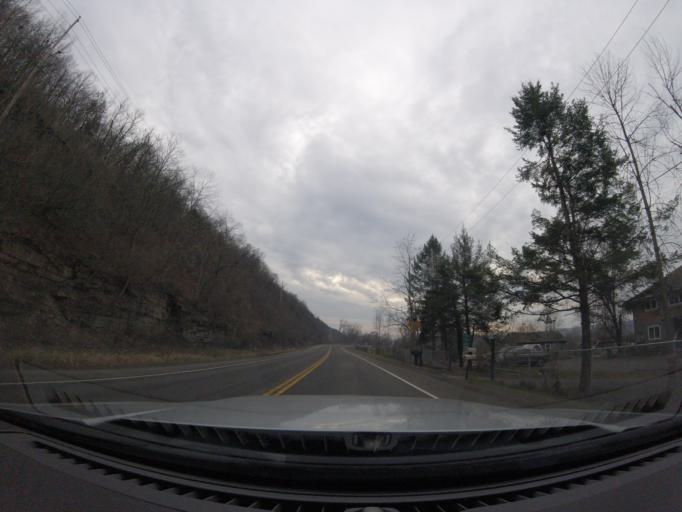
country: US
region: New York
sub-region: Schuyler County
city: Watkins Glen
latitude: 42.3898
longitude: -76.8555
